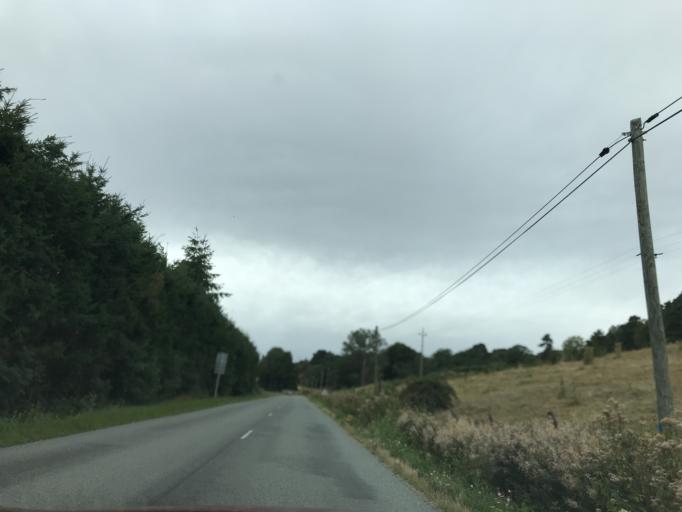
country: FR
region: Rhone-Alpes
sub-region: Departement de la Loire
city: Sail-sous-Couzan
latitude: 45.7002
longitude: 3.9243
